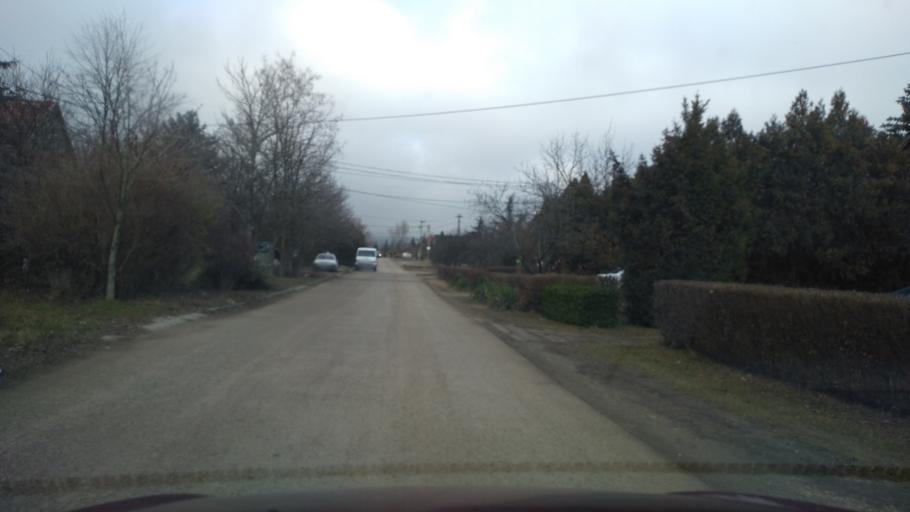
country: HU
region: Pest
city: Szentendre
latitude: 47.6854
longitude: 19.0477
